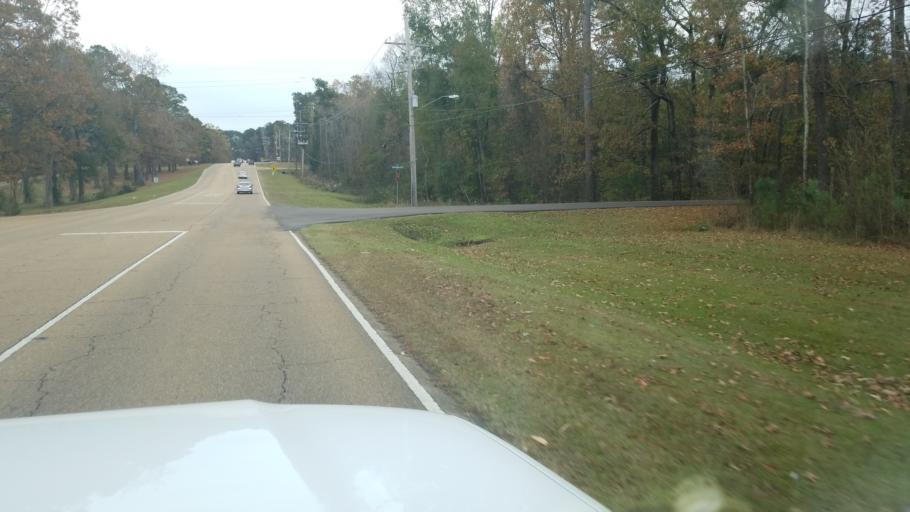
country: US
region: Mississippi
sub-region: Rankin County
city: Brandon
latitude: 32.3739
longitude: -90.0206
